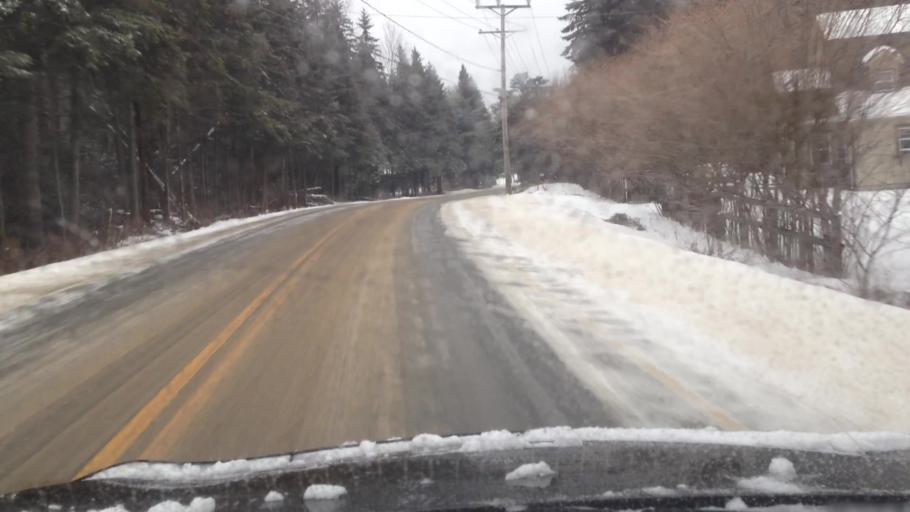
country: CA
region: Quebec
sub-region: Laurentides
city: Mont-Tremblant
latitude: 46.0432
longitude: -74.6074
